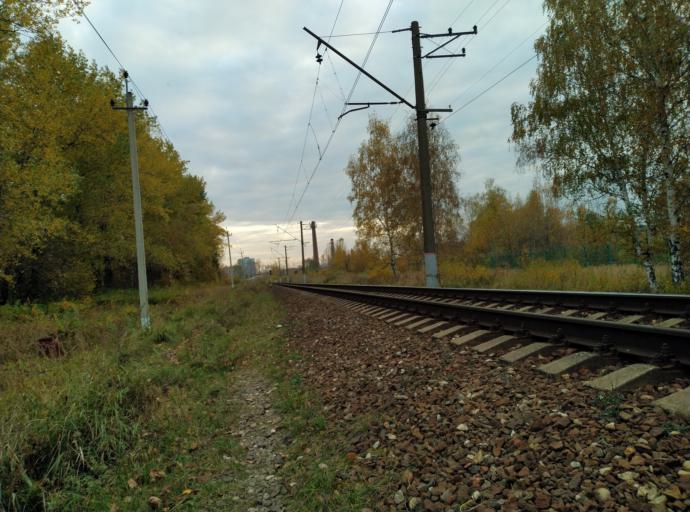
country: RU
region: Moskovskaya
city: Bol'shiye Vyazemy
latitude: 55.6198
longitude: 36.9733
